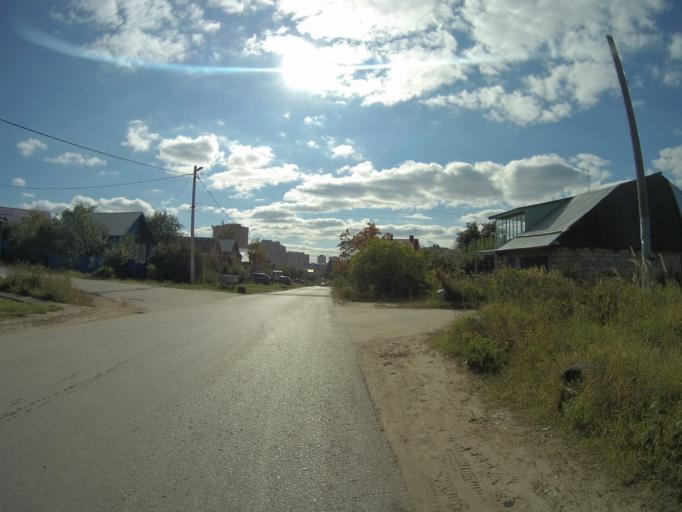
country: RU
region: Vladimir
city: Vladimir
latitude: 56.1114
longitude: 40.3630
